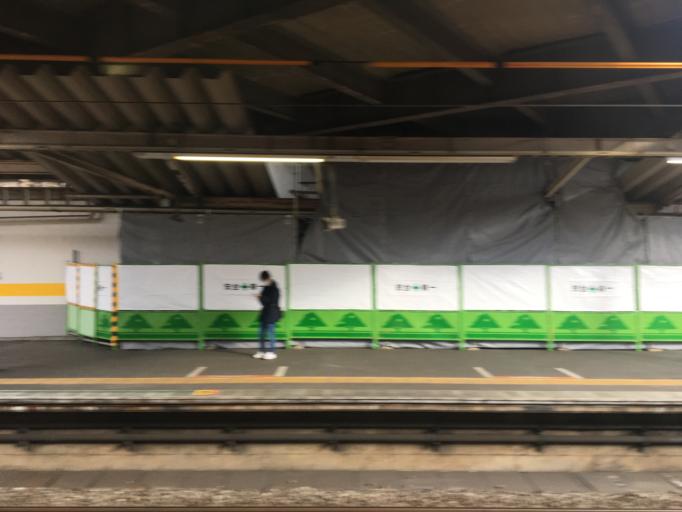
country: JP
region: Saitama
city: Tokorozawa
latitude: 35.7788
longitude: 139.4942
